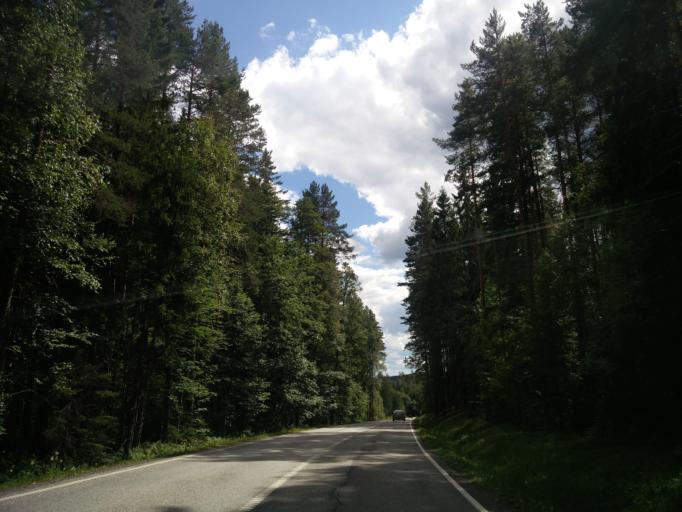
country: SE
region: OErebro
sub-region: Ljusnarsbergs Kommun
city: Kopparberg
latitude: 59.8477
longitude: 14.9977
